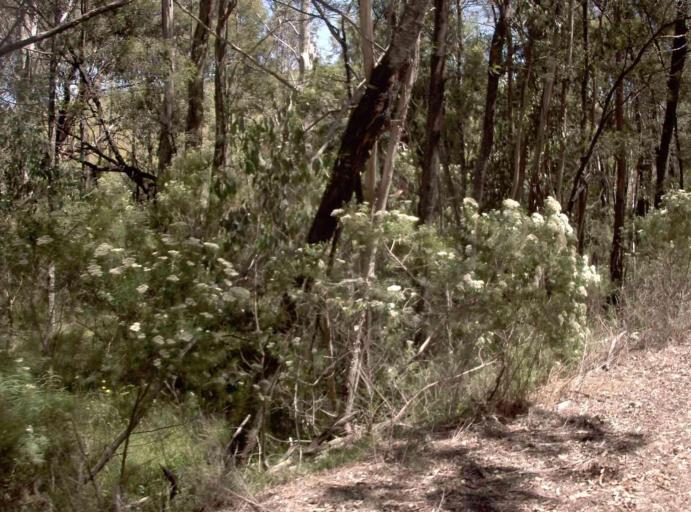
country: AU
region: Victoria
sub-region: East Gippsland
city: Lakes Entrance
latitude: -37.3525
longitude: 148.2280
